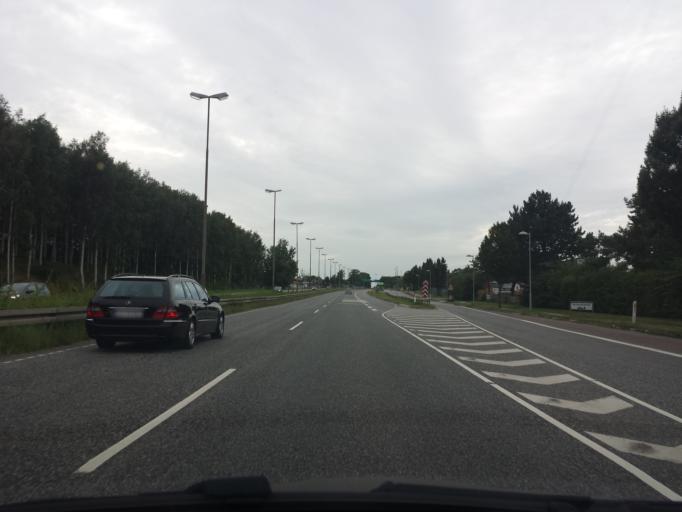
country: DK
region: Capital Region
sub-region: Hoje-Taastrup Kommune
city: Flong
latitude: 55.6519
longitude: 12.2272
